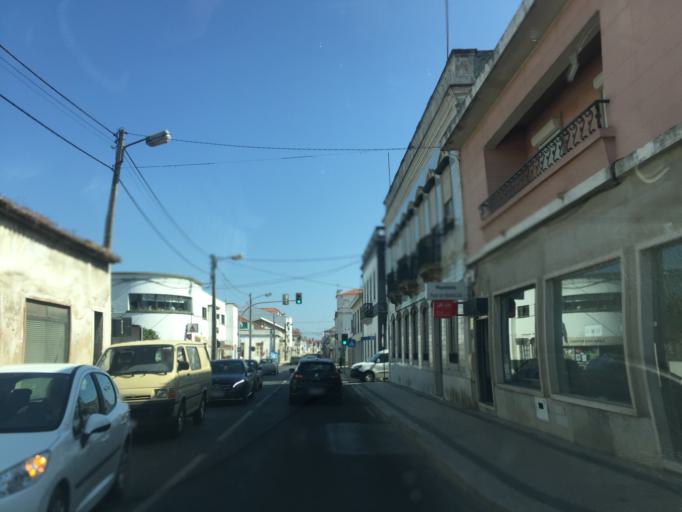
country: PT
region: Santarem
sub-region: Alpiarca
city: Alpiarca
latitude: 39.2601
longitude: -8.5842
